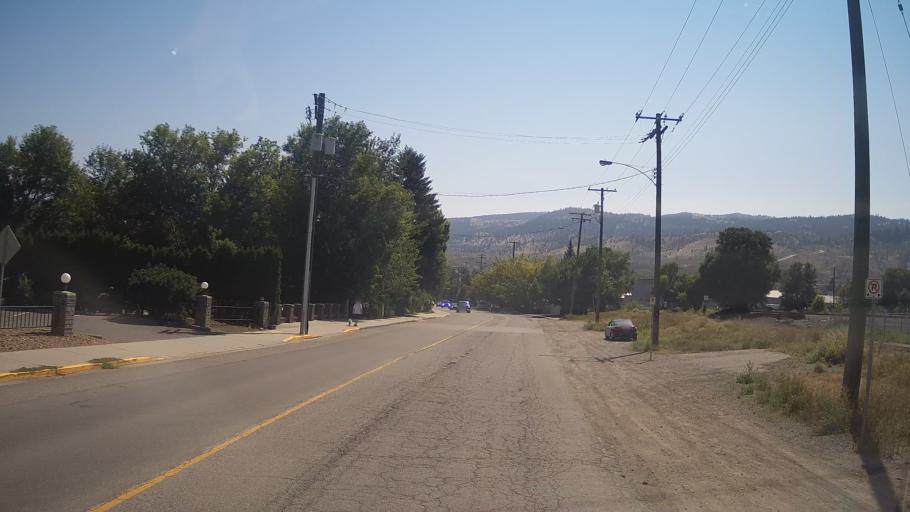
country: CA
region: British Columbia
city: Kamloops
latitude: 50.6769
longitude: -120.3199
